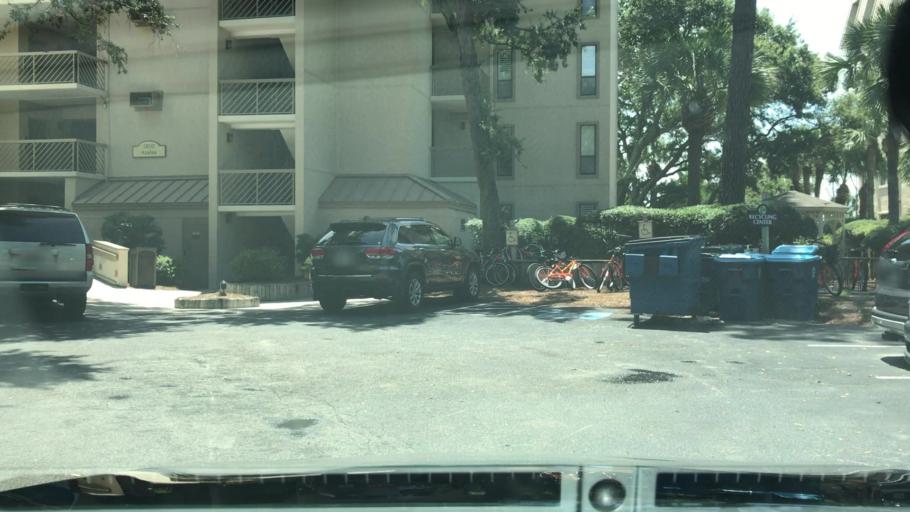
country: US
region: South Carolina
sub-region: Beaufort County
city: Hilton Head Island
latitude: 32.1248
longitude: -80.7883
